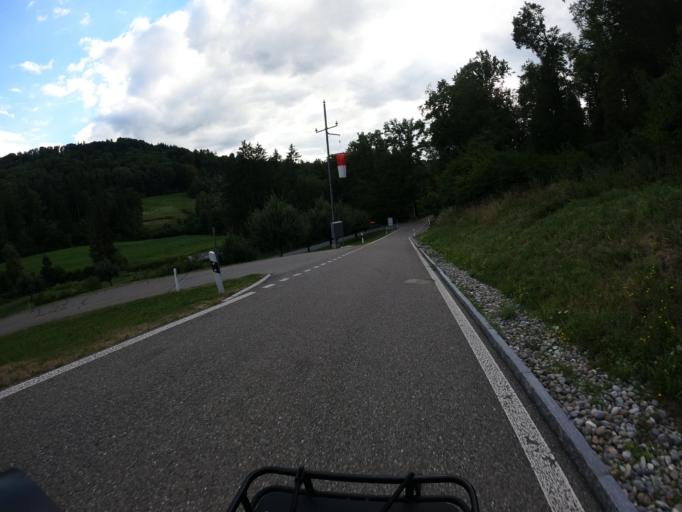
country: CH
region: Aargau
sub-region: Bezirk Bremgarten
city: Rudolfstetten
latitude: 47.3752
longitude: 8.4006
